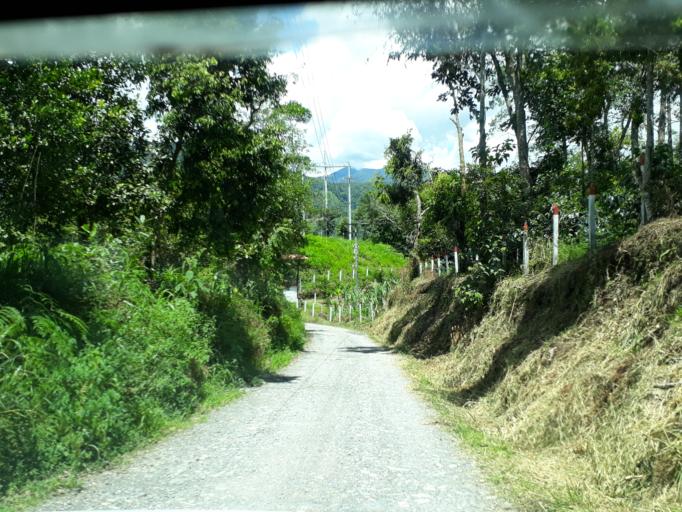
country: CO
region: Cundinamarca
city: Topaipi
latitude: 5.3594
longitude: -74.1982
